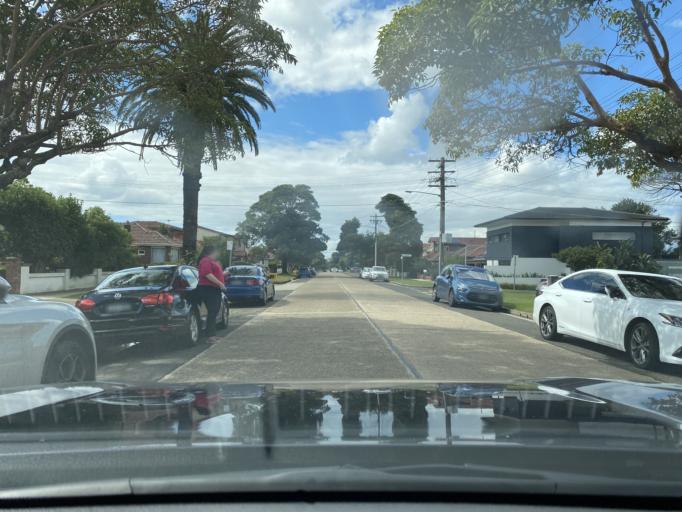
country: AU
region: New South Wales
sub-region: Canada Bay
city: Wareemba
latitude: -33.8662
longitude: 151.1414
